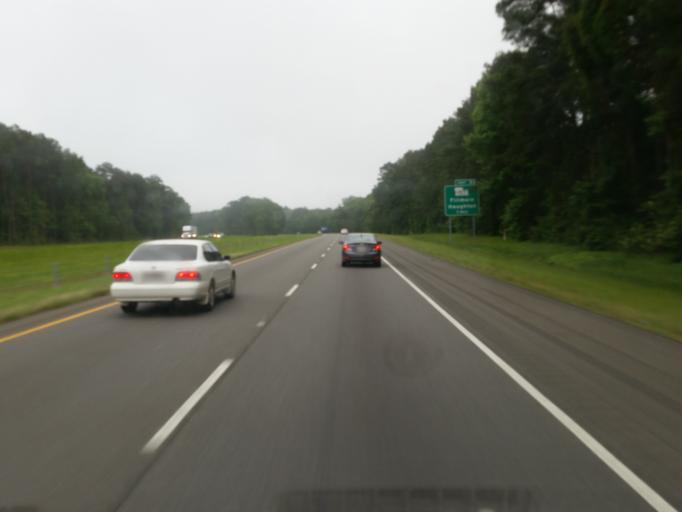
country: US
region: Louisiana
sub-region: Bossier Parish
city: Haughton
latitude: 32.5417
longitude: -93.5358
